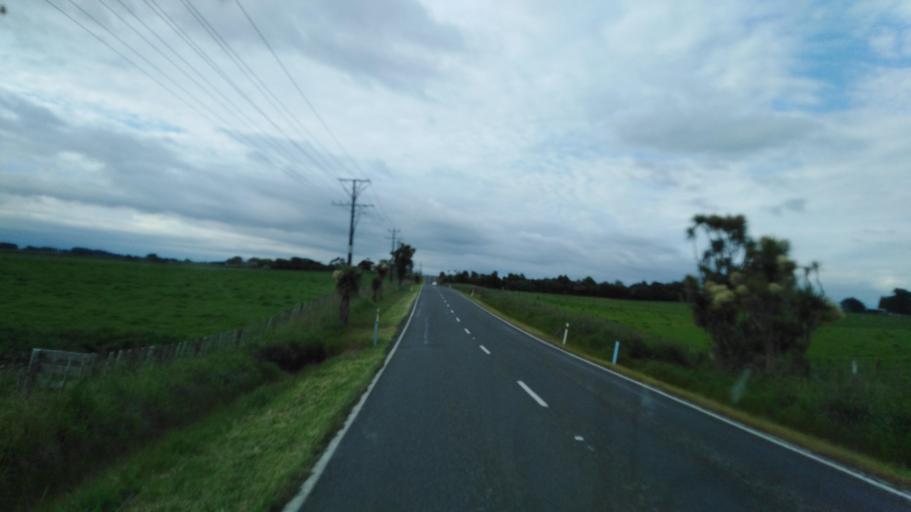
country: NZ
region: Manawatu-Wanganui
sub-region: Rangitikei District
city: Bulls
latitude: -40.1053
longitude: 175.3605
